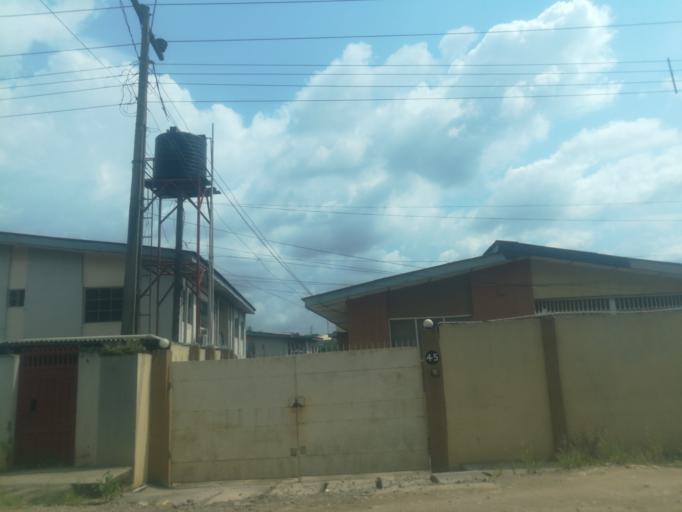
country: NG
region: Oyo
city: Ibadan
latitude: 7.3620
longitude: 3.8556
